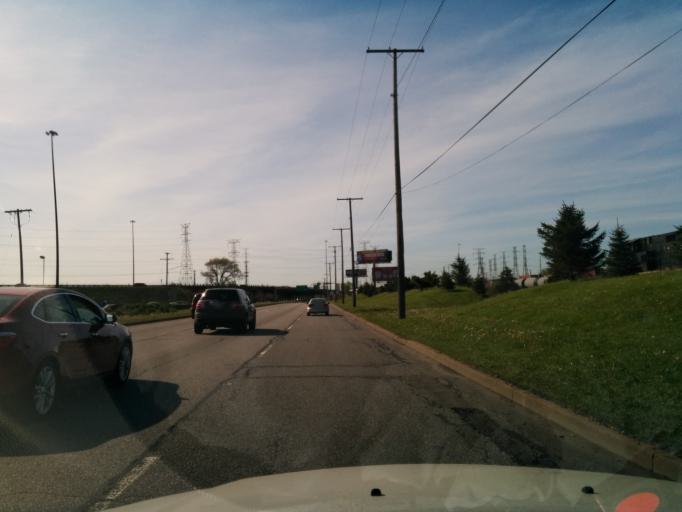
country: US
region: Indiana
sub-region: Lake County
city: Whiting
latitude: 41.6990
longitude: -87.5201
